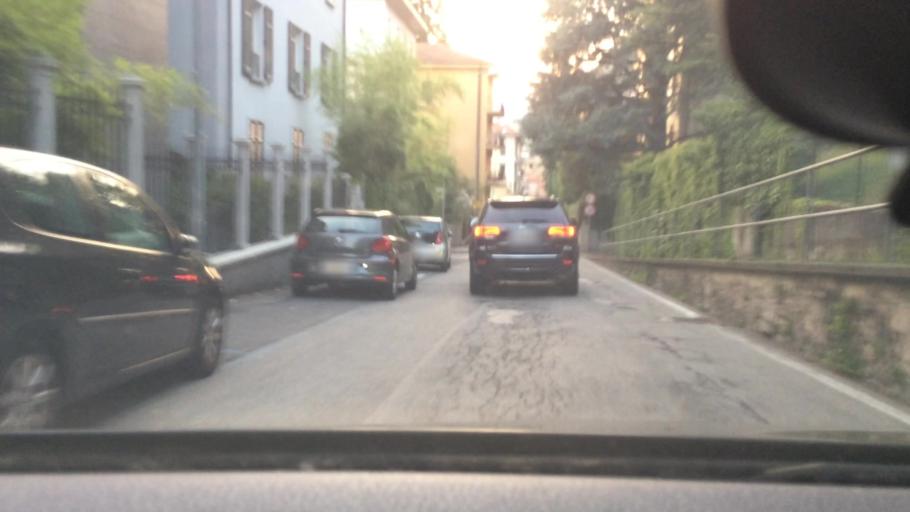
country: IT
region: Lombardy
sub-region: Provincia di Como
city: Brunate
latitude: 45.8109
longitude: 9.0924
